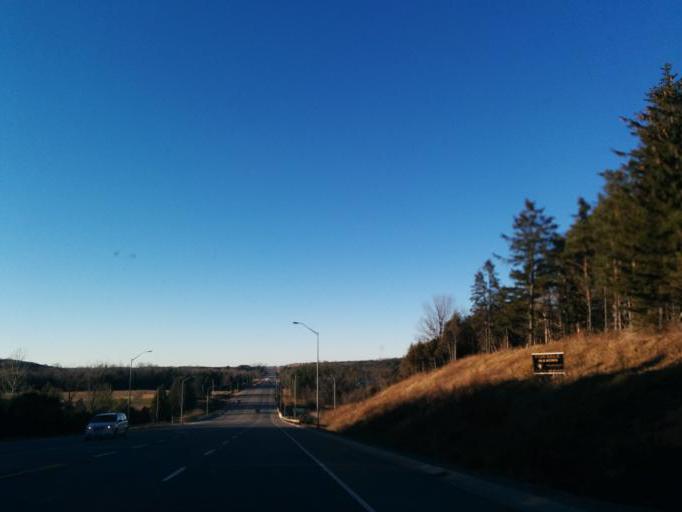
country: CA
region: Ontario
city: Orangeville
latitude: 43.9003
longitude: -80.0503
